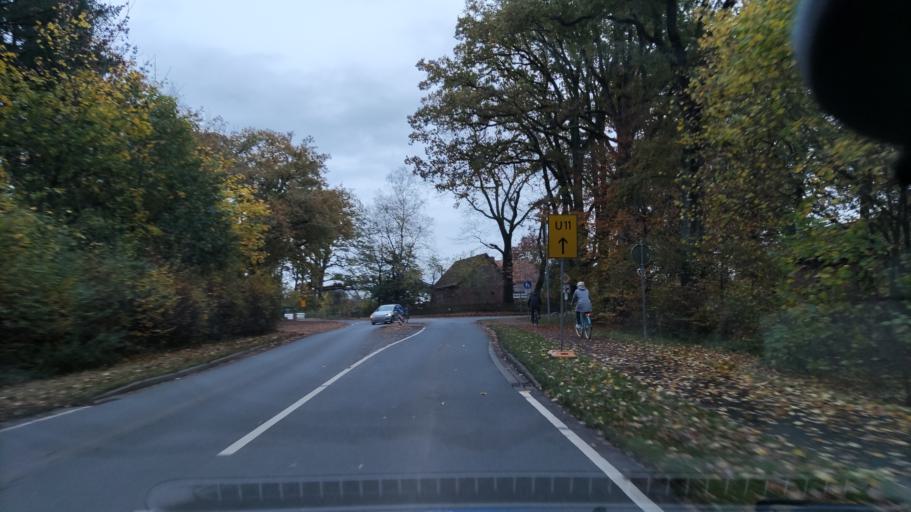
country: DE
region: Lower Saxony
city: Munster
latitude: 53.0155
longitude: 10.0856
